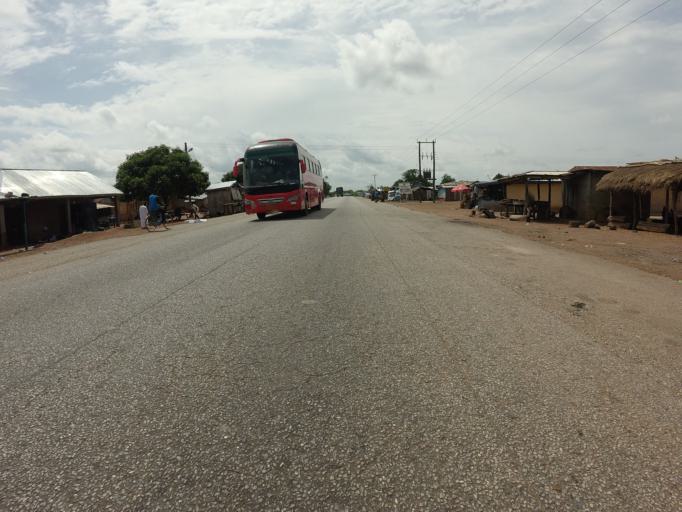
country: GH
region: Brong-Ahafo
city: Kintampo
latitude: 8.4493
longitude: -1.5652
